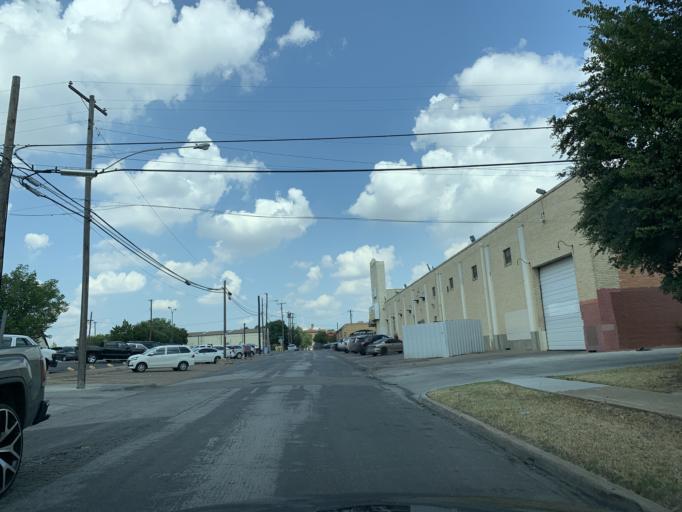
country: US
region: Texas
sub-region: Dallas County
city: Dallas
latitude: 32.7438
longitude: -96.8198
